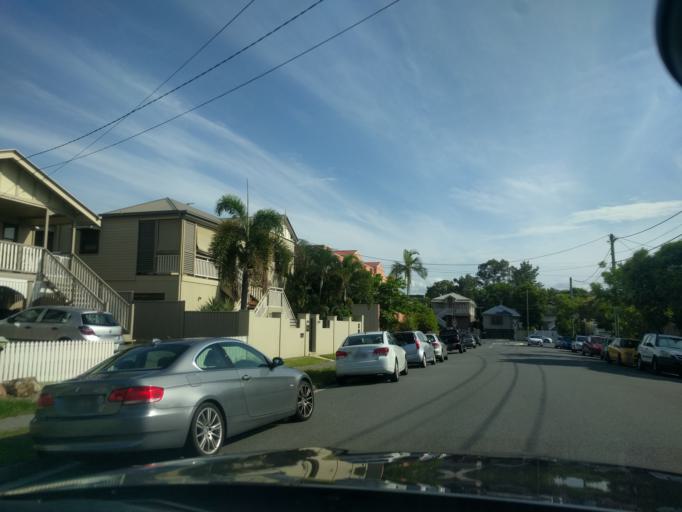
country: AU
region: Queensland
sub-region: Brisbane
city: Greenslopes
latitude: -27.5045
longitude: 153.0461
